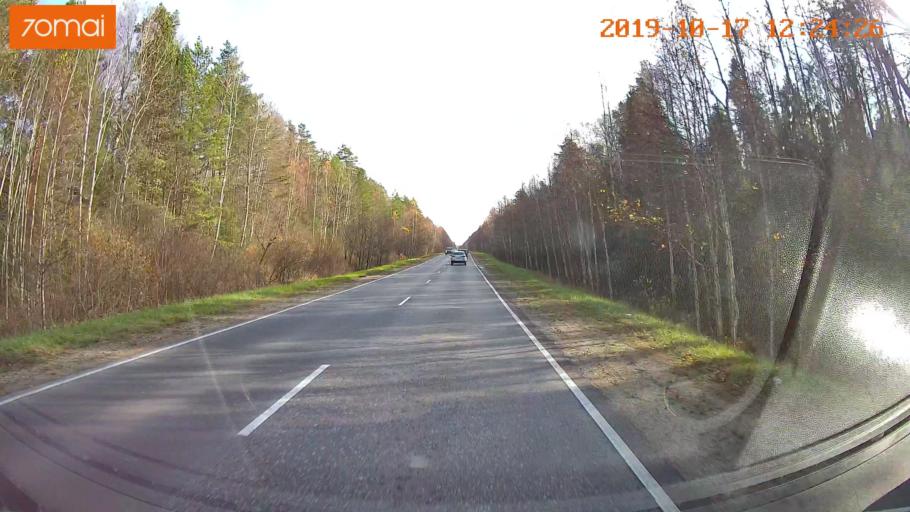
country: RU
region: Rjazan
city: Gus'-Zheleznyy
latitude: 55.0355
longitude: 41.2149
